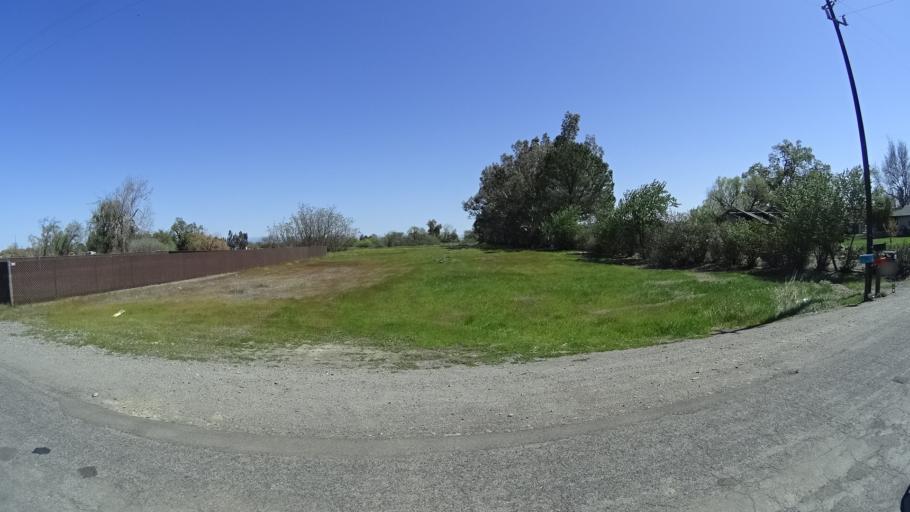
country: US
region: California
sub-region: Glenn County
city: Orland
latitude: 39.7735
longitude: -122.2387
